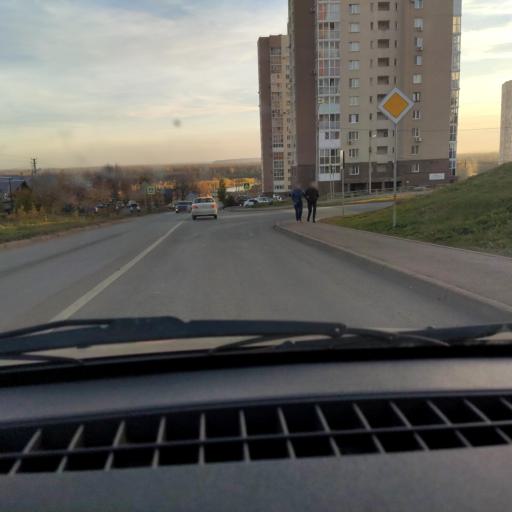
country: RU
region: Bashkortostan
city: Ufa
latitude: 54.6892
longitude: 55.9978
